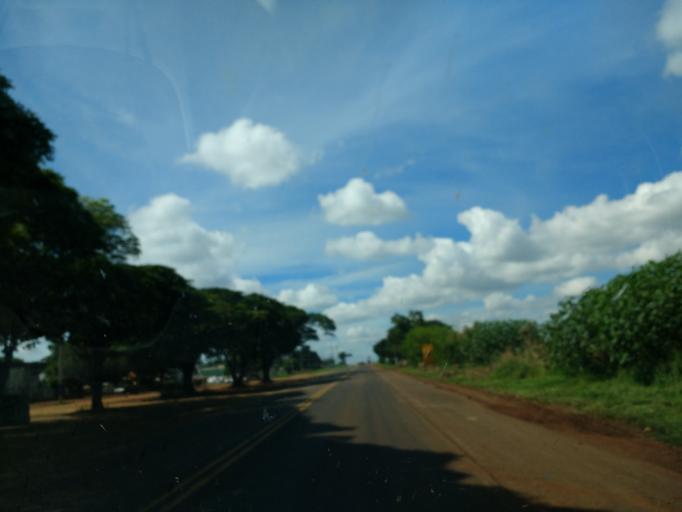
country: BR
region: Parana
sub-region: Paicandu
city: Paicandu
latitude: -23.4670
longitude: -52.0568
